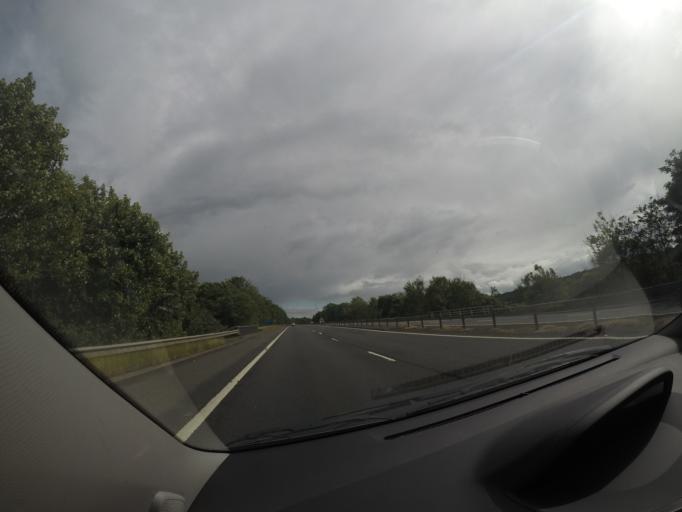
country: GB
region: Scotland
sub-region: Falkirk
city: Dunipace
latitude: 56.0502
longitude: -3.9201
